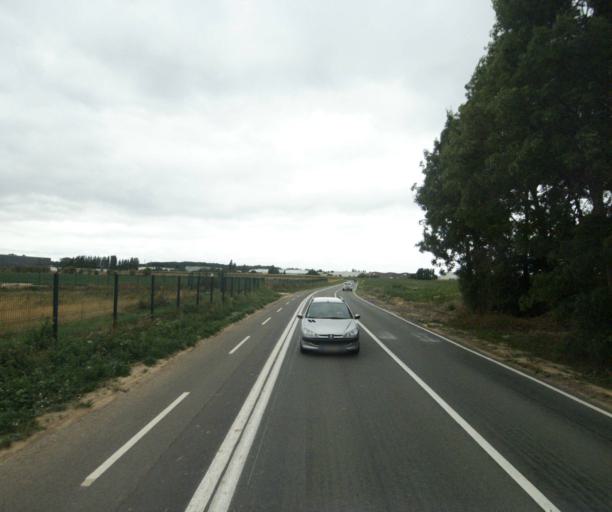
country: FR
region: Nord-Pas-de-Calais
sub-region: Departement du Nord
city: Lesquin
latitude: 50.5713
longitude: 3.1217
